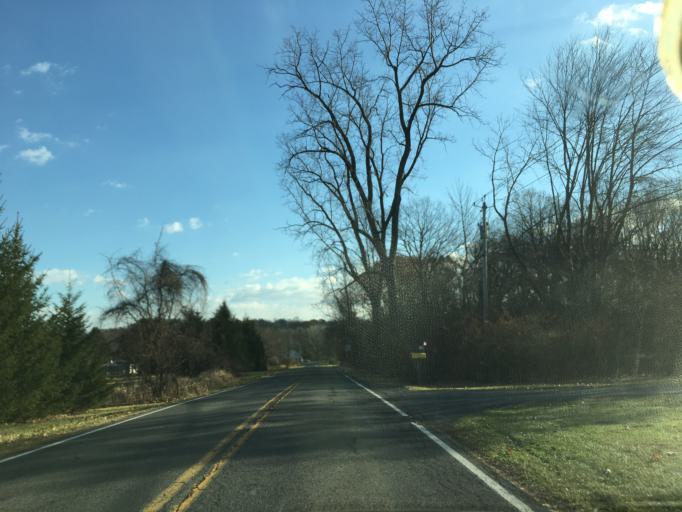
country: US
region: New York
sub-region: Rensselaer County
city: Hampton Manor
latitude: 42.6307
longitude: -73.6901
